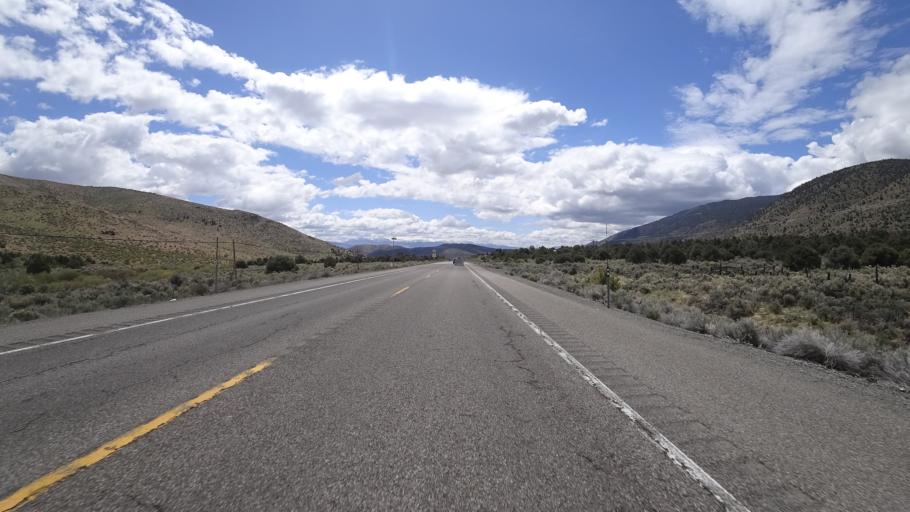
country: US
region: Nevada
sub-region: Douglas County
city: Gardnerville Ranchos
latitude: 38.7465
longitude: -119.5666
